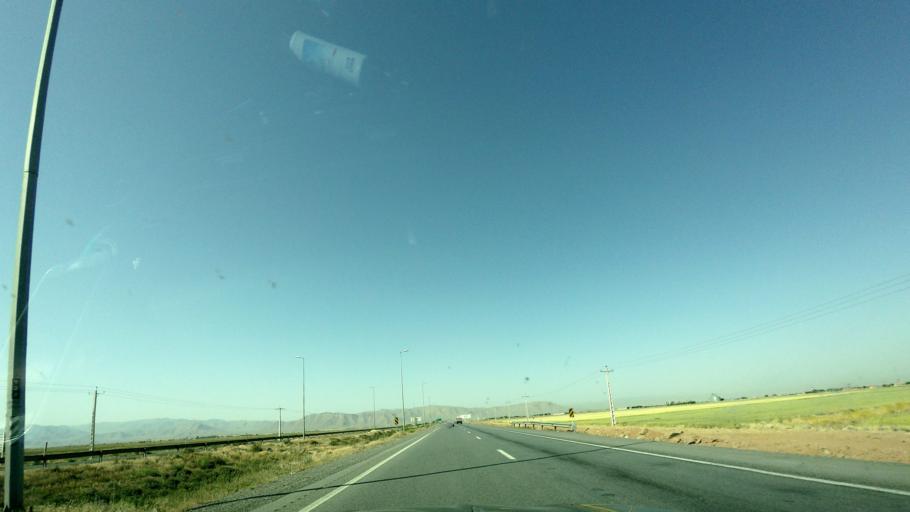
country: IR
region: Markazi
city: Ashtian
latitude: 34.1998
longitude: 50.0603
